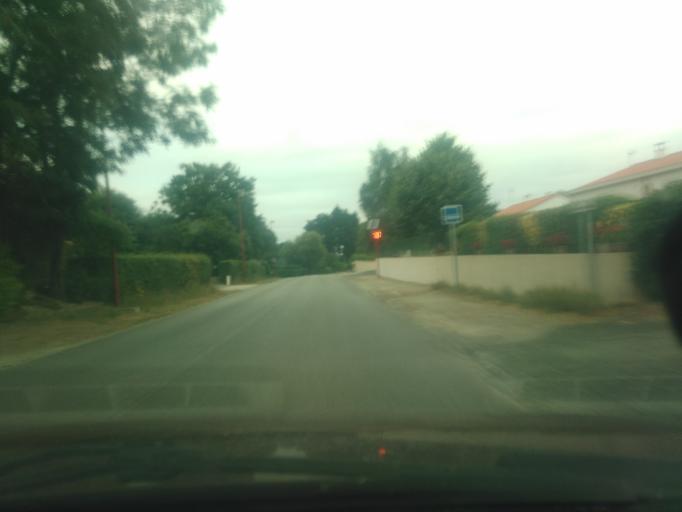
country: FR
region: Pays de la Loire
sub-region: Departement de la Vendee
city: Saint-Denis-la-Chevasse
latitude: 46.7904
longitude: -1.3161
